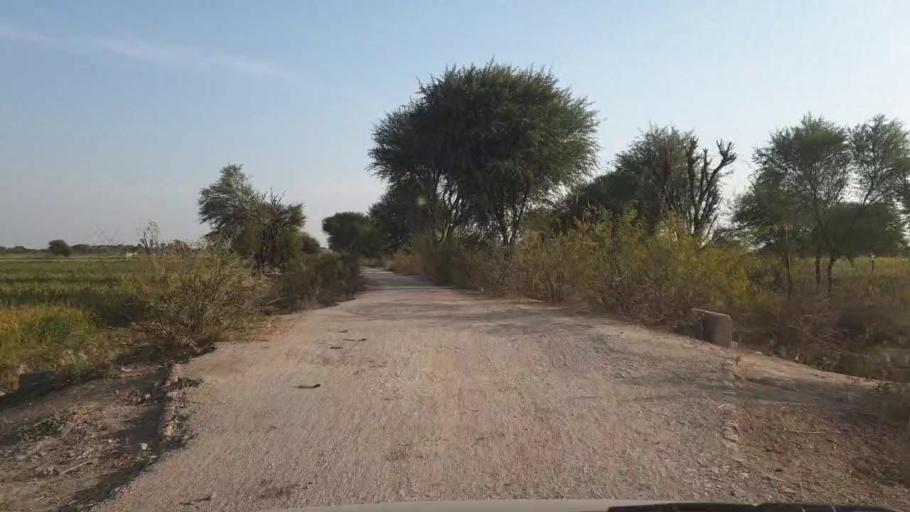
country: PK
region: Sindh
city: Chambar
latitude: 25.2395
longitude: 68.7903
